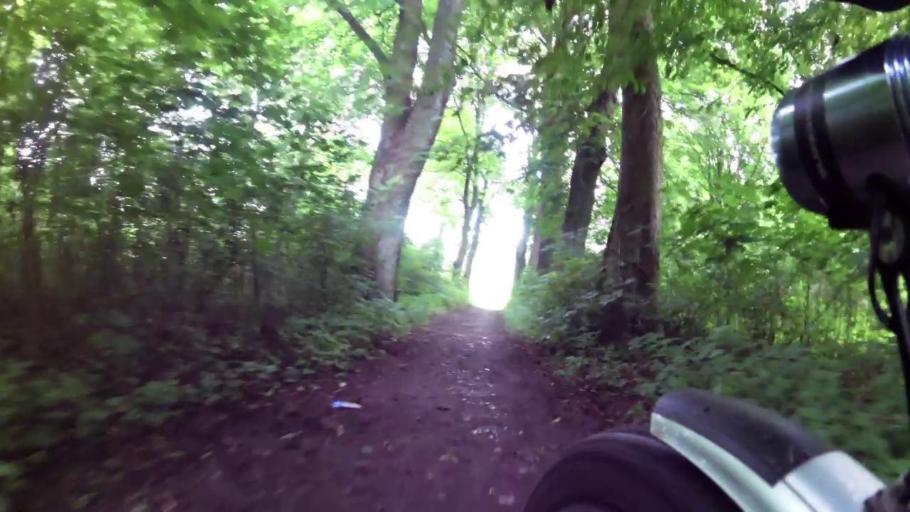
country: PL
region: West Pomeranian Voivodeship
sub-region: Powiat lobeski
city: Lobez
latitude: 53.7001
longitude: 15.6066
